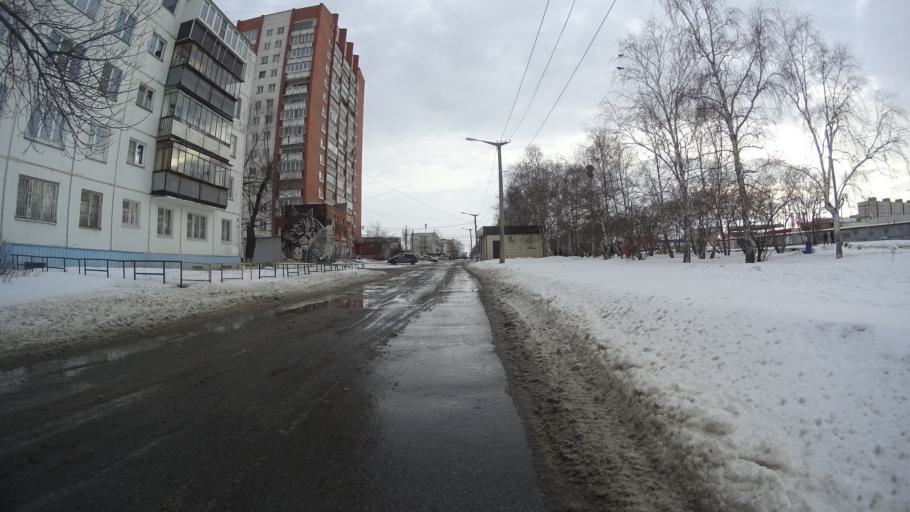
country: RU
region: Chelyabinsk
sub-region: Gorod Chelyabinsk
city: Chelyabinsk
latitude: 55.1956
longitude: 61.3222
